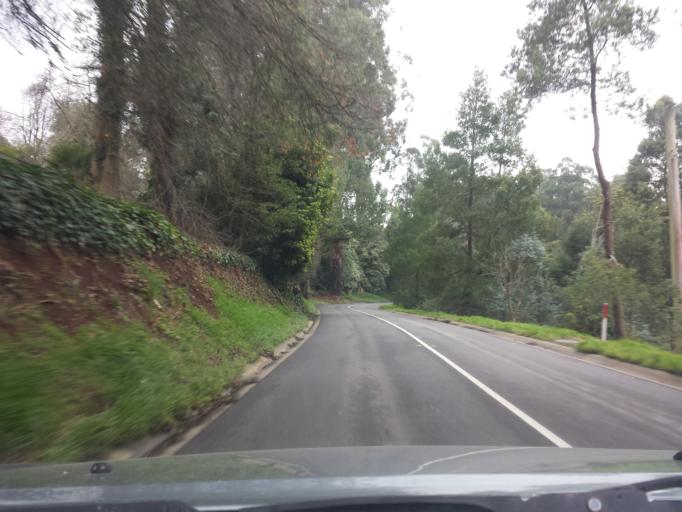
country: AU
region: Victoria
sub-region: Yarra Ranges
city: Monbulk
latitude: -37.8764
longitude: 145.3982
